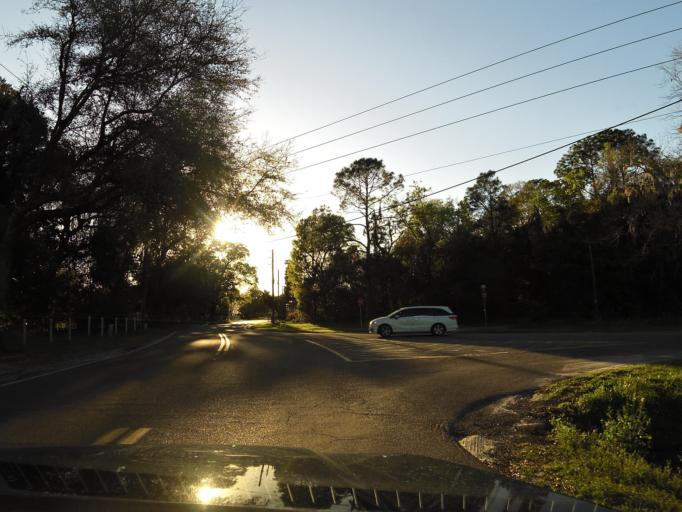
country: US
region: Florida
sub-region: Bradford County
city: Starke
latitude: 29.8646
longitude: -82.1303
